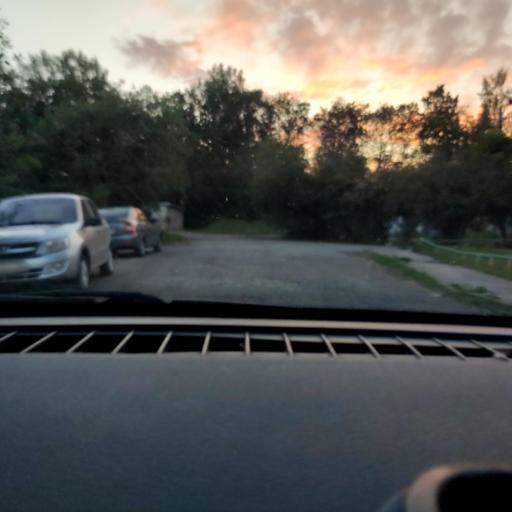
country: RU
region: Perm
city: Kukushtan
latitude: 57.6346
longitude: 56.5283
